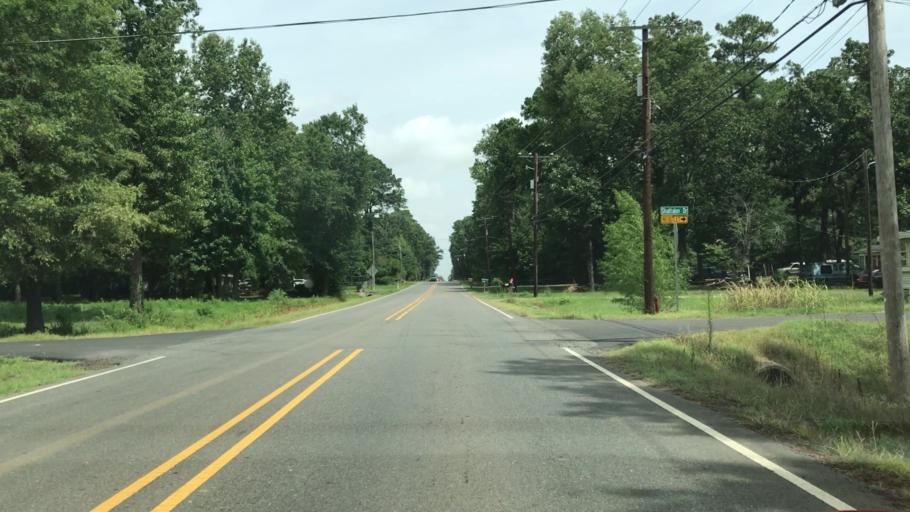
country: US
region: Louisiana
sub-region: De Soto Parish
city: Stonewall
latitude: 32.3781
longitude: -93.7635
